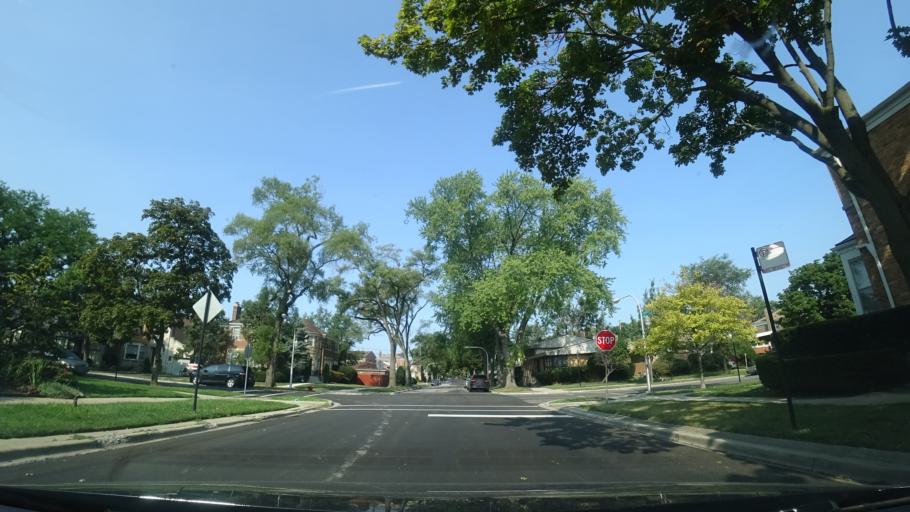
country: US
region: Illinois
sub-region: Cook County
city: Lincolnwood
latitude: 41.9938
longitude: -87.7161
